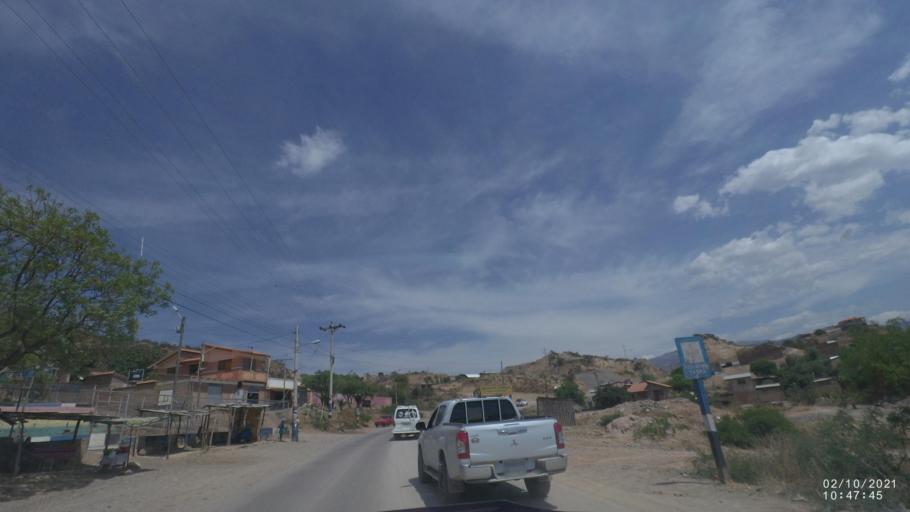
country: BO
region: Cochabamba
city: Sipe Sipe
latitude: -17.5825
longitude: -66.3316
